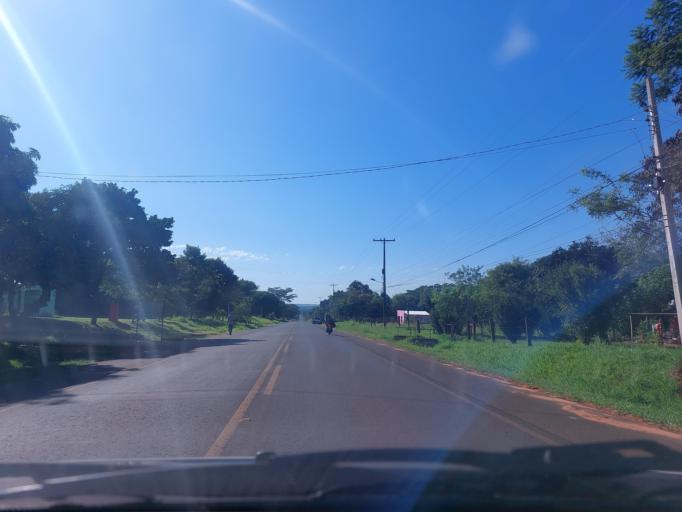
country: PY
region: San Pedro
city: Guayaybi
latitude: -24.5313
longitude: -56.4244
